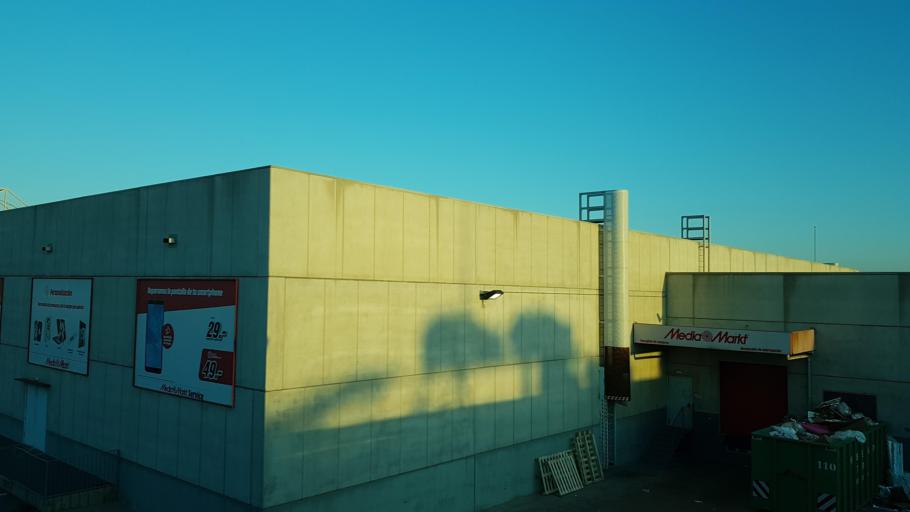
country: ES
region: Valencia
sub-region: Provincia de Valencia
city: Aldaia
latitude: 39.4751
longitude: -0.4838
